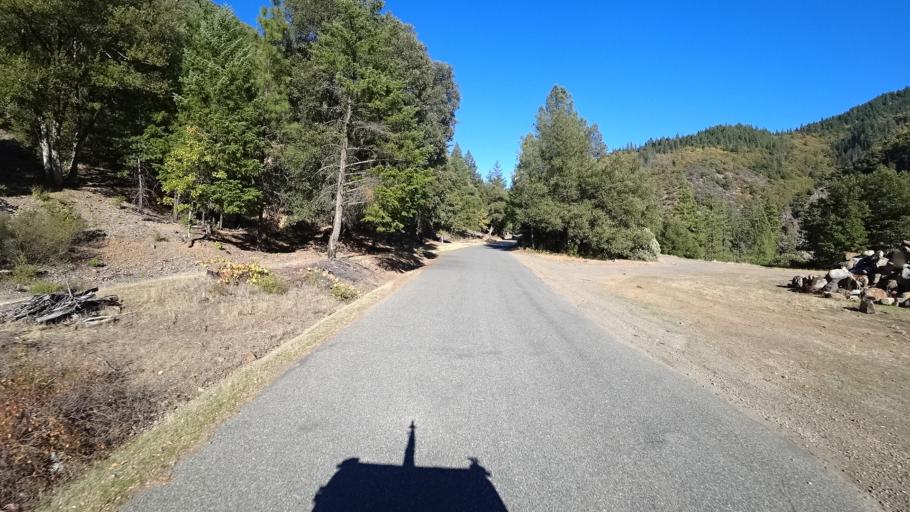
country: US
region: California
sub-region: Humboldt County
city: Willow Creek
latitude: 41.2656
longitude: -123.3091
